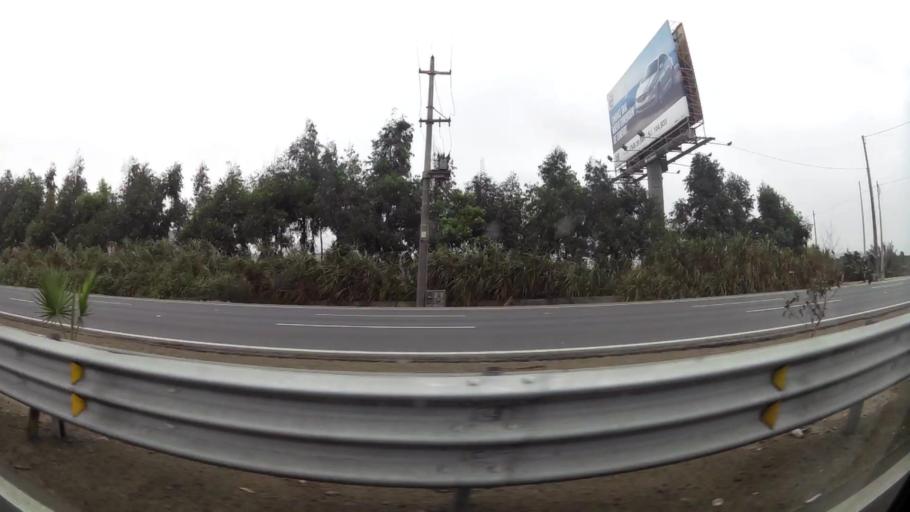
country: PE
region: Lima
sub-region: Lima
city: Punta Hermosa
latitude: -12.2695
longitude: -76.9003
